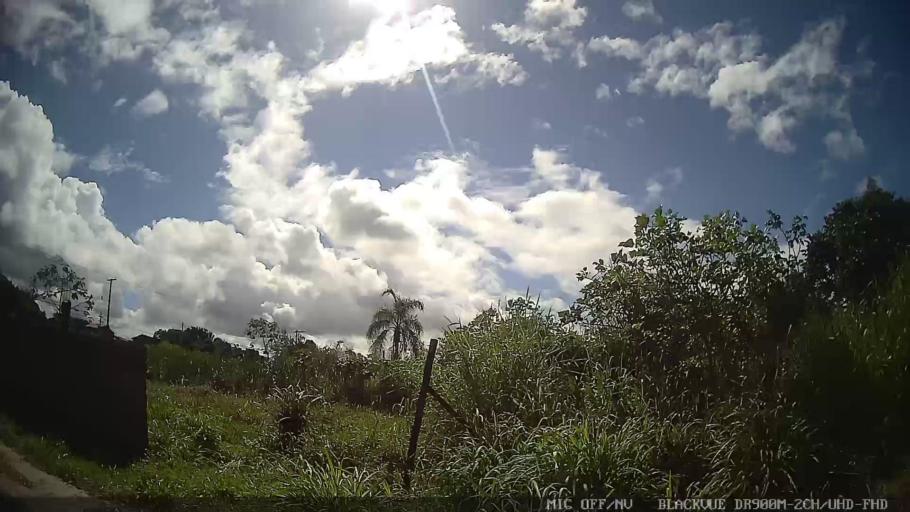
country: BR
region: Sao Paulo
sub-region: Itanhaem
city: Itanhaem
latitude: -24.2224
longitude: -46.8662
